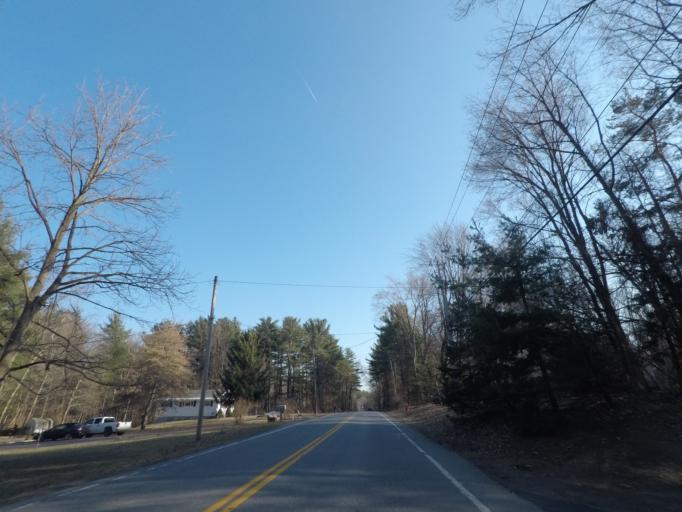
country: US
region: New York
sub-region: Saratoga County
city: Country Knolls
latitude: 42.8369
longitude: -73.7764
